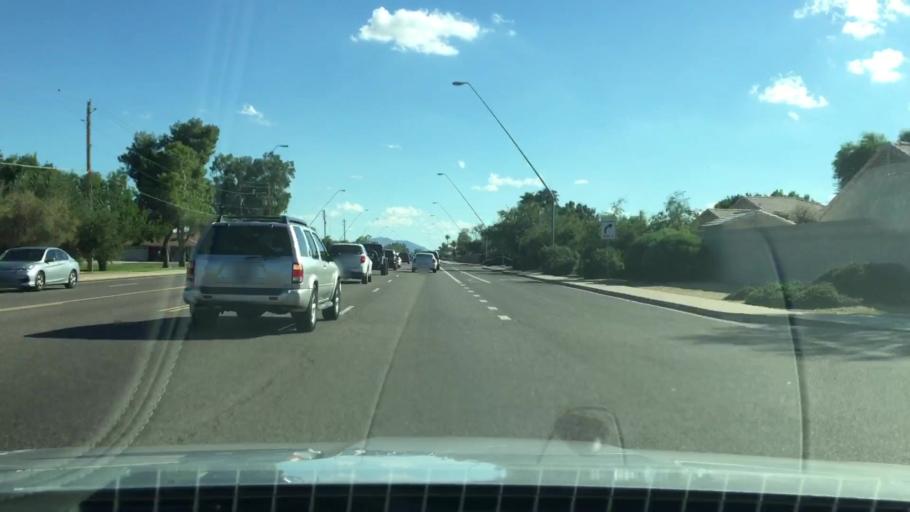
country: US
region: Arizona
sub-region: Maricopa County
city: Gilbert
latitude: 33.4026
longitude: -111.7193
